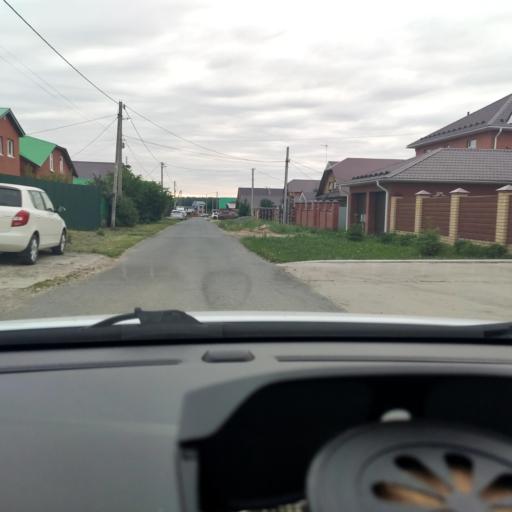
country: RU
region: Tatarstan
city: Vysokaya Gora
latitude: 55.9130
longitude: 49.3321
